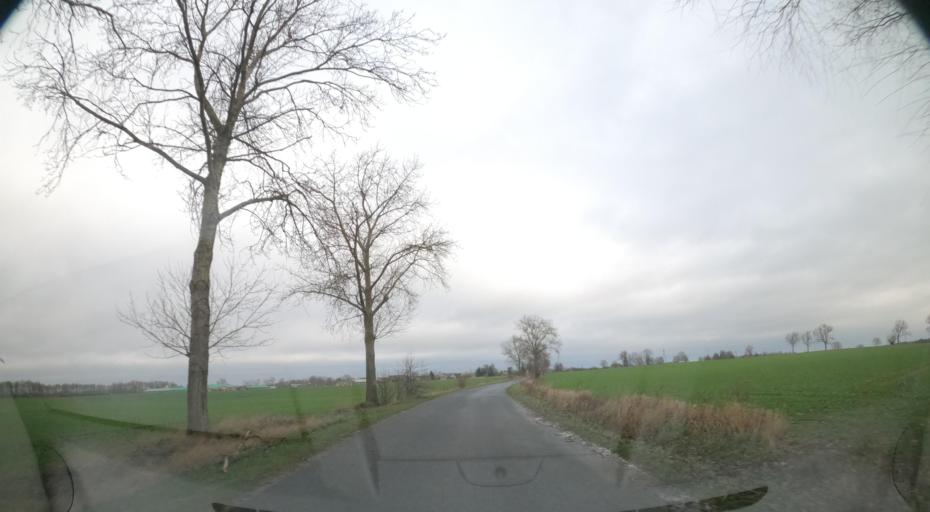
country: PL
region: Greater Poland Voivodeship
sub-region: Powiat pilski
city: Wysoka
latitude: 53.2539
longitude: 17.1504
